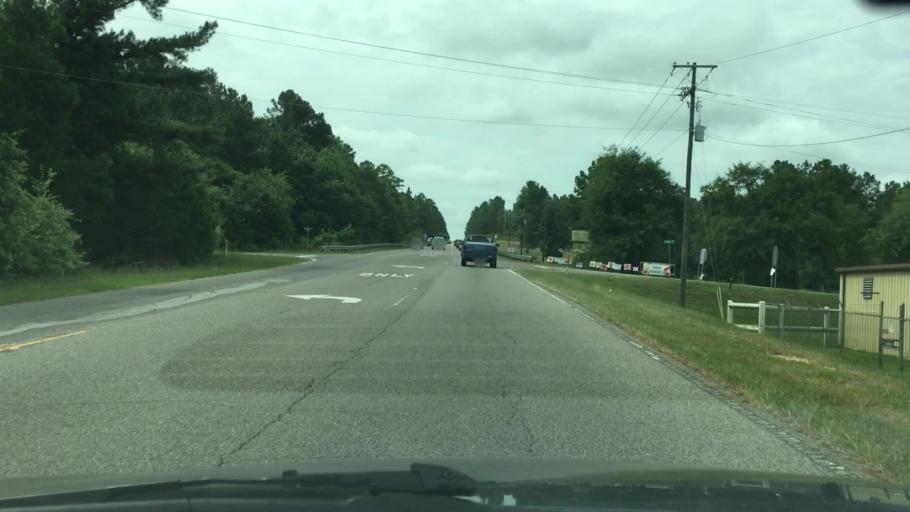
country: US
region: South Carolina
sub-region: Aiken County
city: Warrenville
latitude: 33.5554
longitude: -81.7787
